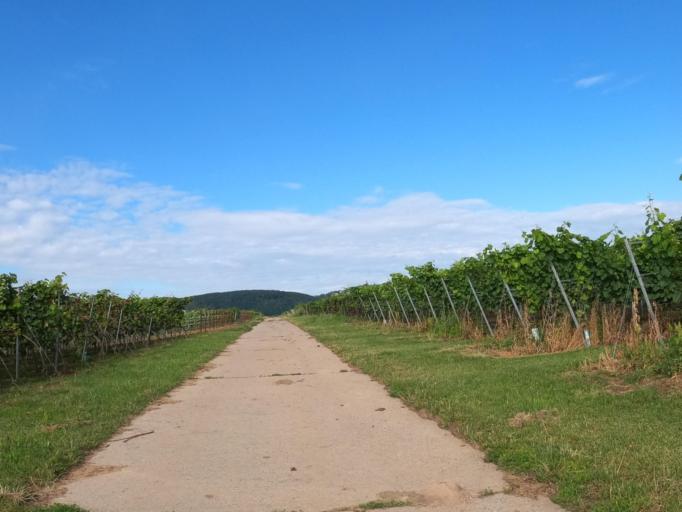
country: DE
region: Rheinland-Pfalz
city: Kirchheim an der Weinstrasse
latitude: 49.5318
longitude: 8.1732
